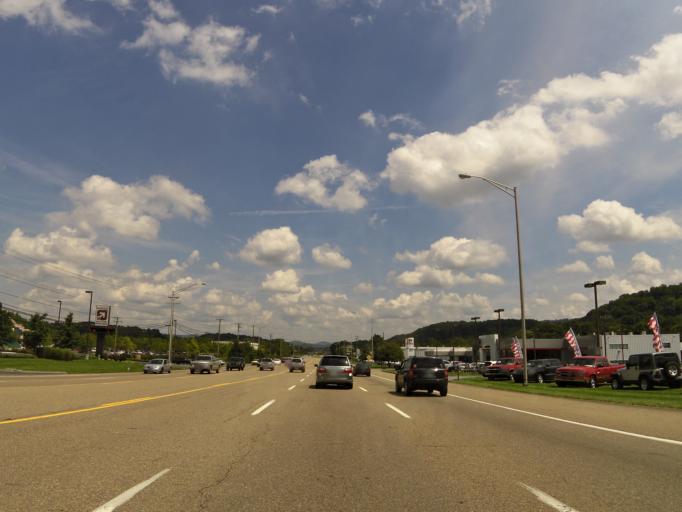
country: US
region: Tennessee
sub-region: Sullivan County
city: Bloomingdale
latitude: 36.5464
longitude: -82.5022
